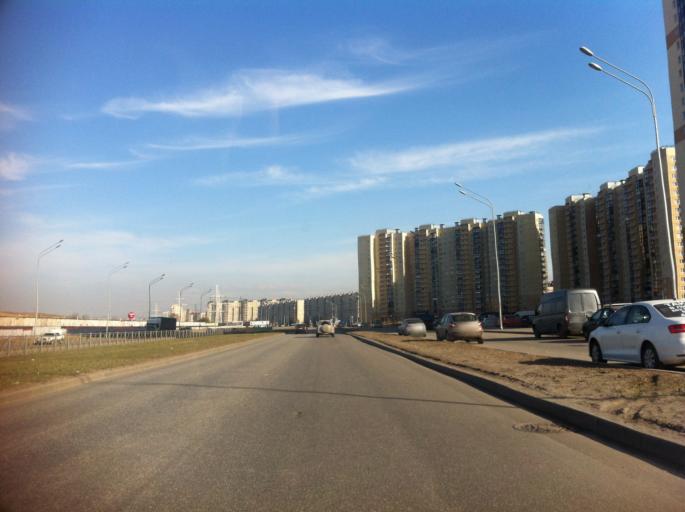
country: RU
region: St.-Petersburg
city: Uritsk
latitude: 59.8622
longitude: 30.1967
